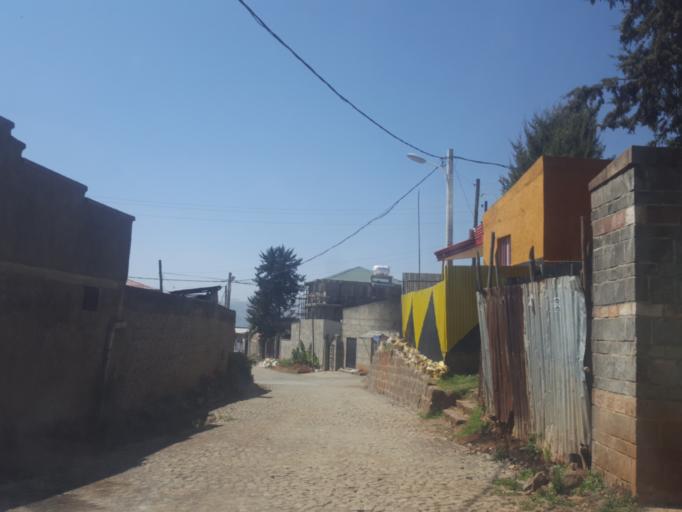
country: ET
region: Adis Abeba
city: Addis Ababa
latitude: 9.0576
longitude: 38.7247
